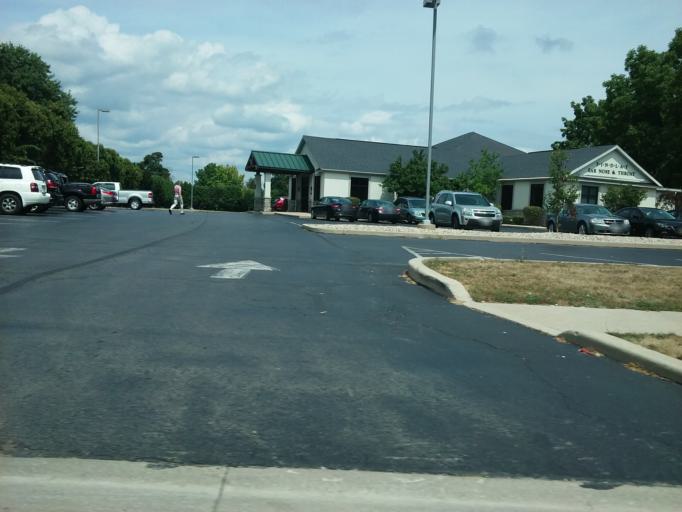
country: US
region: Ohio
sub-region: Hancock County
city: Findlay
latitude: 41.0411
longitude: -83.6673
